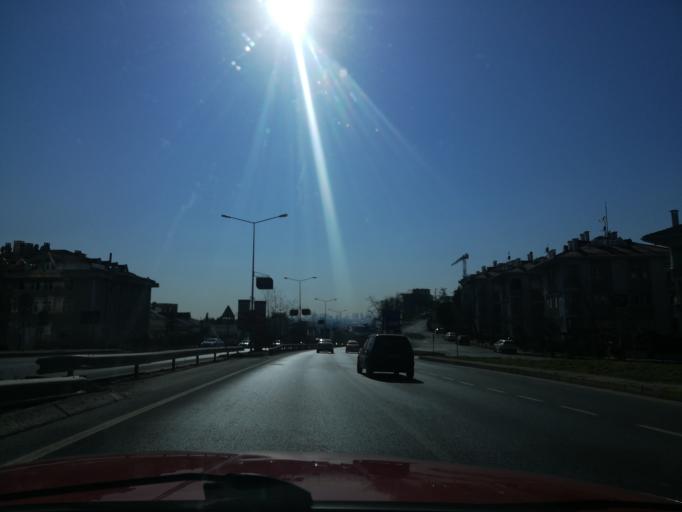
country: TR
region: Istanbul
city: Mahmut Sevket Pasa
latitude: 41.1103
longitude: 29.1158
